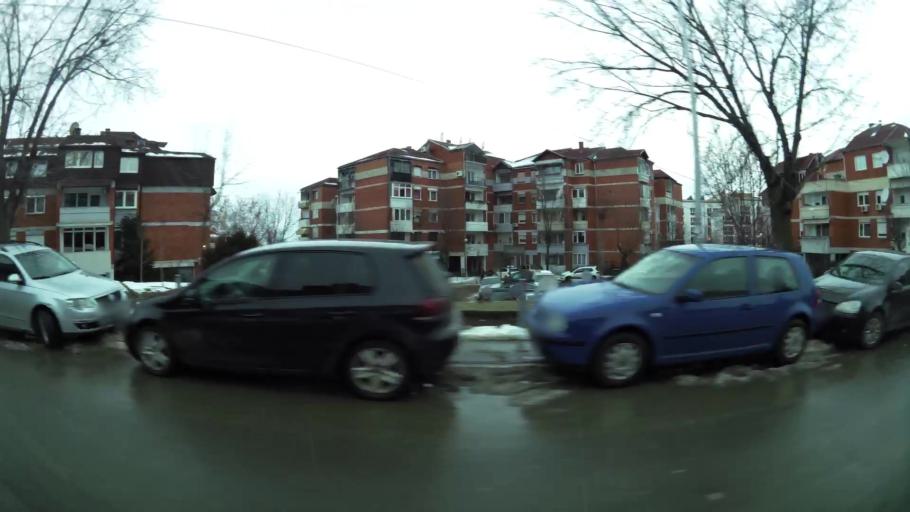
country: XK
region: Pristina
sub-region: Komuna e Prishtines
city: Pristina
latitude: 42.6511
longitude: 21.1672
